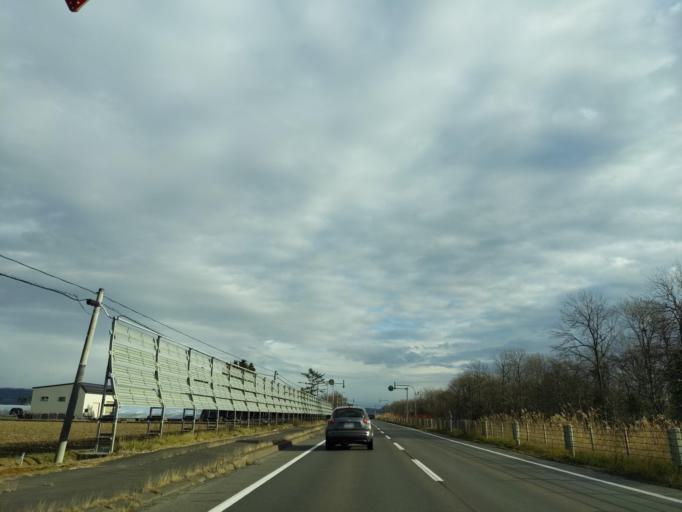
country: JP
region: Hokkaido
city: Kitahiroshima
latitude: 42.9643
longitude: 141.6783
